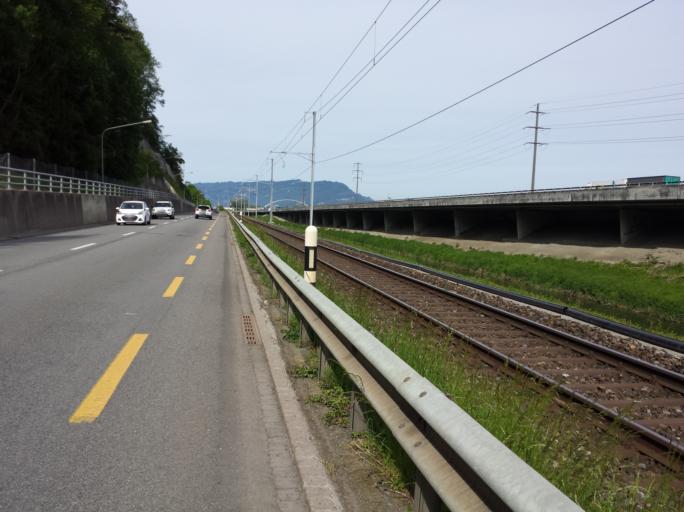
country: CH
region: Saint Gallen
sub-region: Wahlkreis Rheintal
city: Sankt Margrethen
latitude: 47.4416
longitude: 9.6459
